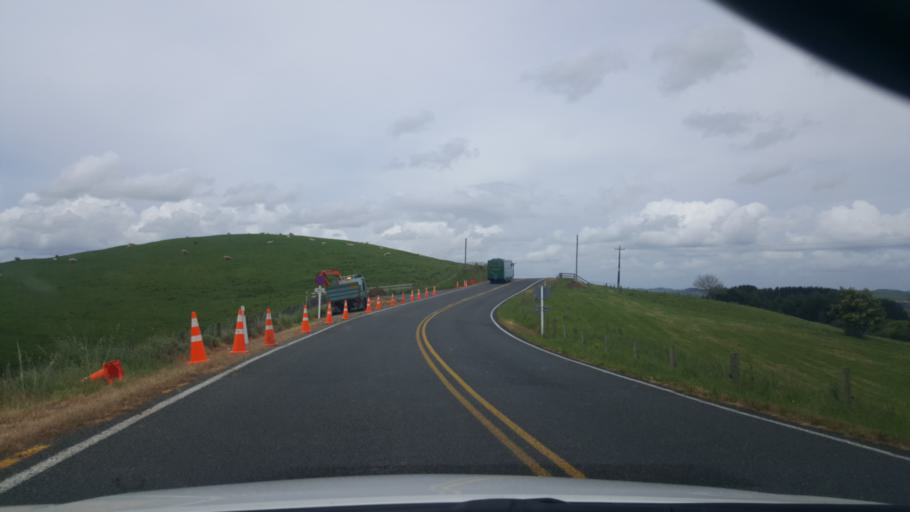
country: NZ
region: Waikato
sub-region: Matamata-Piako District
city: Matamata
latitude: -37.8778
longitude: 175.6880
